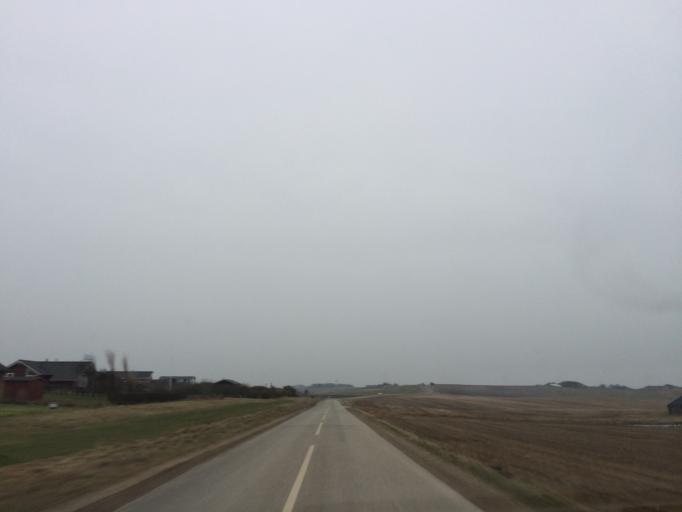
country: DK
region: Central Jutland
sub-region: Lemvig Kommune
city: Lemvig
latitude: 56.5798
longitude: 8.2726
